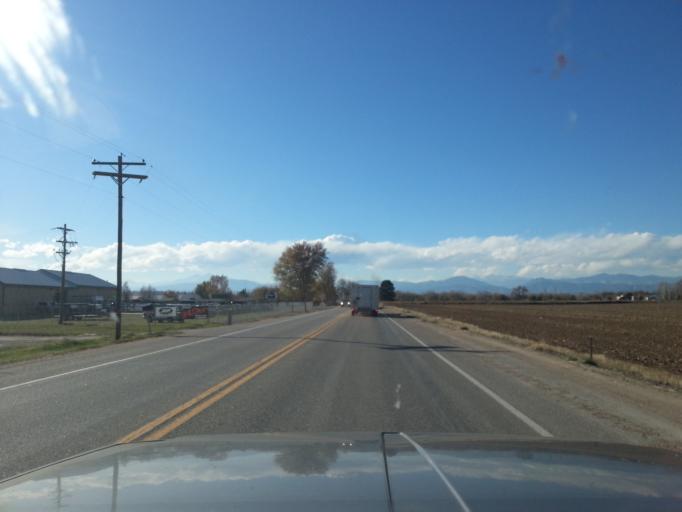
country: US
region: Colorado
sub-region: Larimer County
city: Loveland
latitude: 40.3783
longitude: -105.0468
